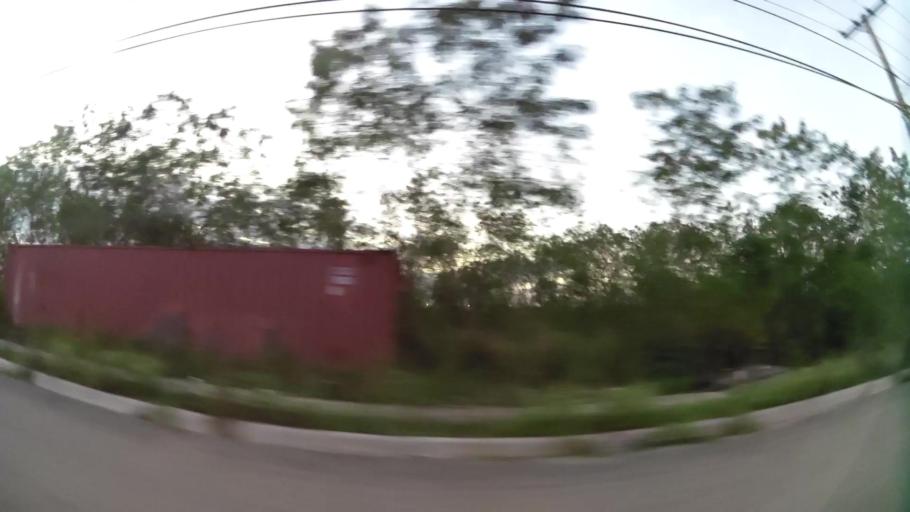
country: DO
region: Nacional
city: La Agustina
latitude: 18.5471
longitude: -69.9425
